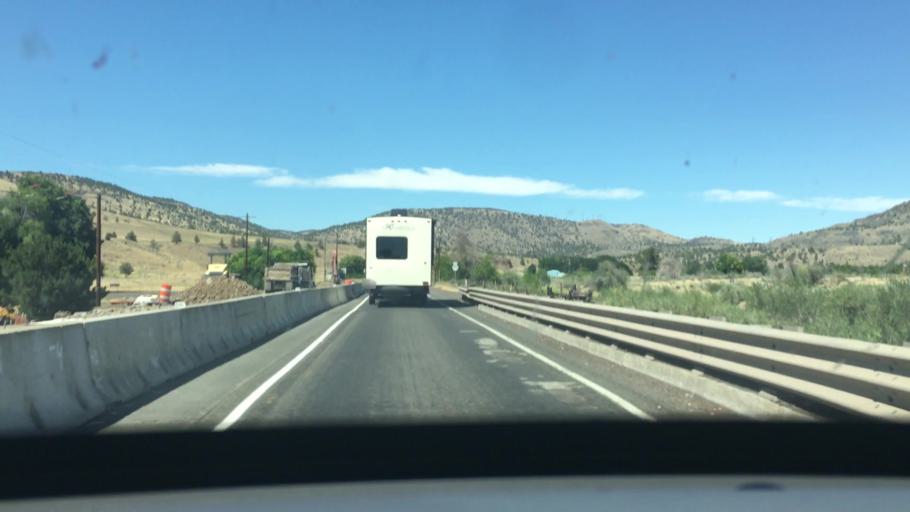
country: US
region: Oregon
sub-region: Jefferson County
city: Madras
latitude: 44.8119
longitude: -120.9326
